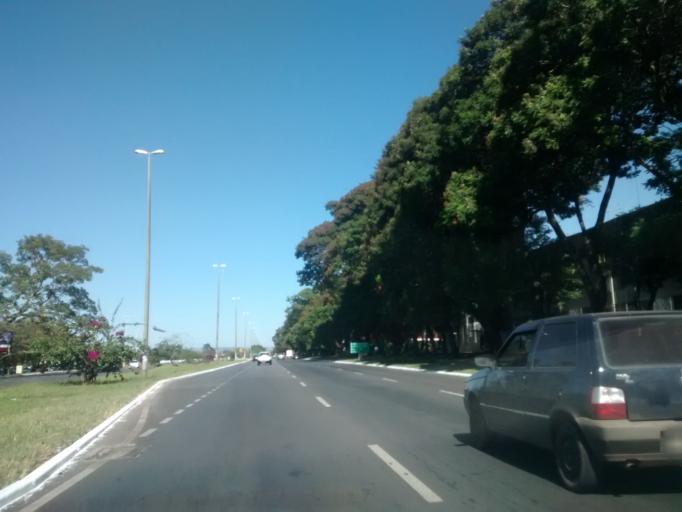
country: BR
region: Federal District
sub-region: Brasilia
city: Brasilia
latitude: -15.8257
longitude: -47.9018
